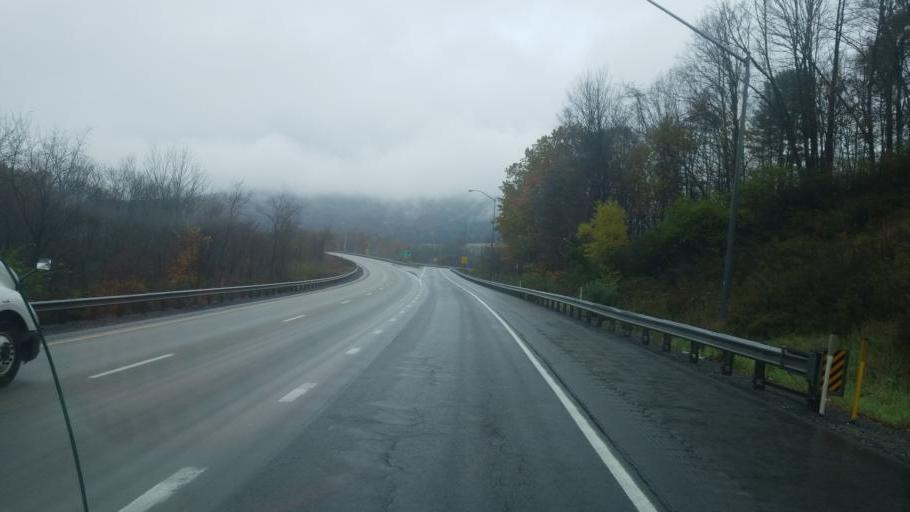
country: US
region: Pennsylvania
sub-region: Centre County
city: Milesburg
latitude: 40.9575
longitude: -77.7788
